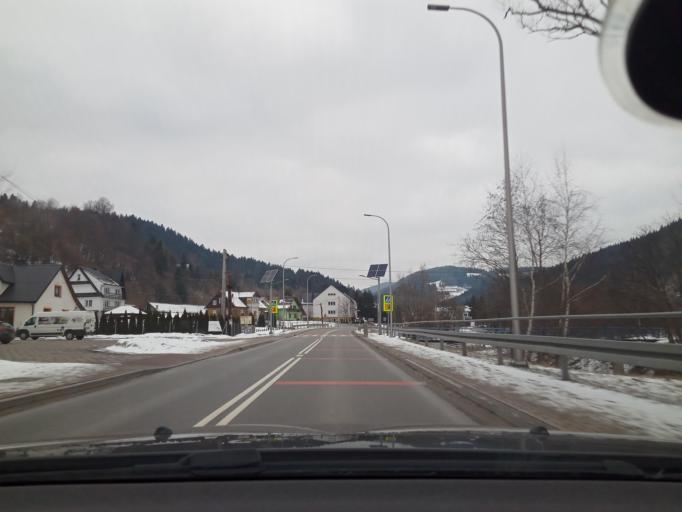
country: PL
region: Lesser Poland Voivodeship
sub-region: Powiat limanowski
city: Kamienica
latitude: 49.6048
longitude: 20.2972
